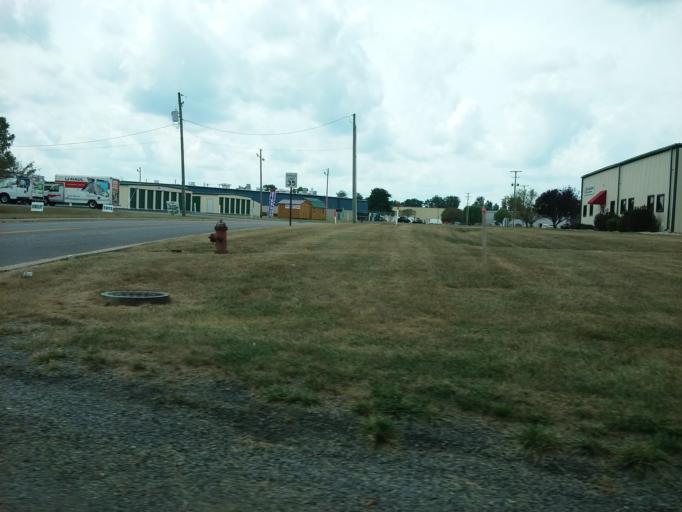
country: US
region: Ohio
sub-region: Hancock County
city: Findlay
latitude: 41.0523
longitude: -83.6730
